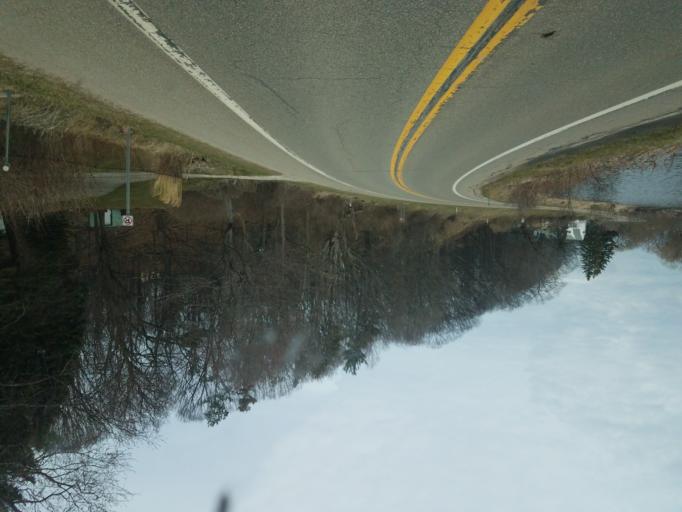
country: US
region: Michigan
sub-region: Oceana County
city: Hart
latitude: 43.7703
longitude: -86.4137
